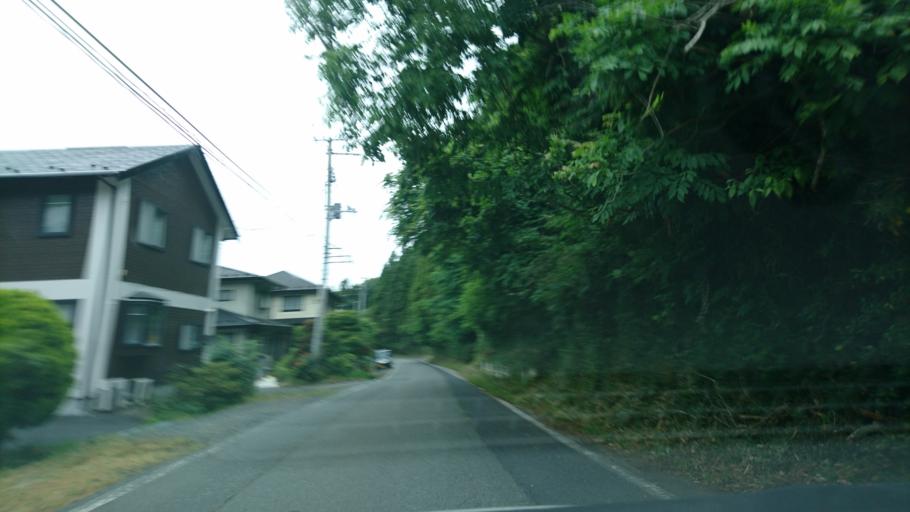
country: JP
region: Iwate
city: Ichinoseki
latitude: 38.9020
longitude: 141.1901
